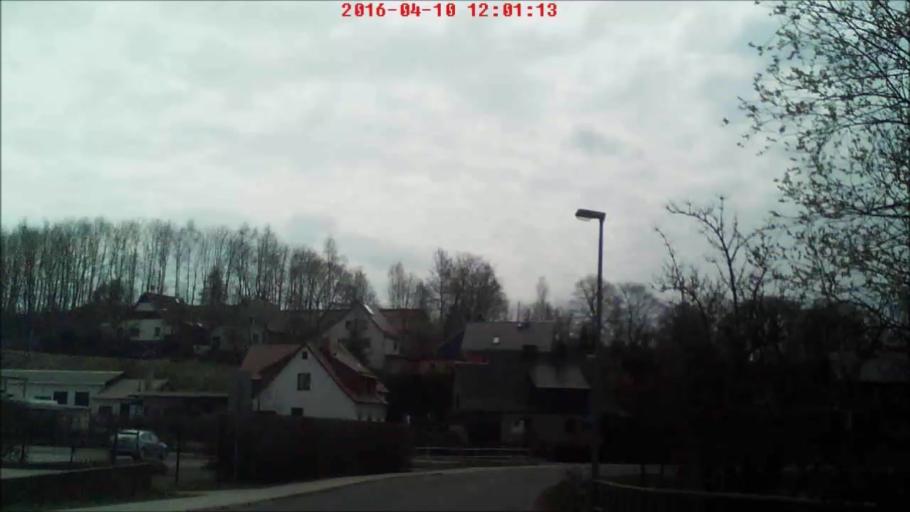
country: DE
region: Thuringia
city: Zella-Mehlis
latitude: 50.6675
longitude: 10.6653
